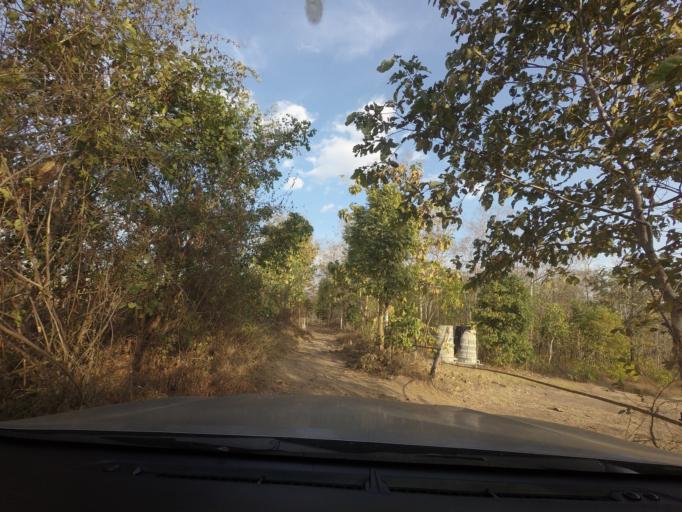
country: TH
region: Mae Hong Son
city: Mae Hi
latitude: 19.3400
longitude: 98.4282
